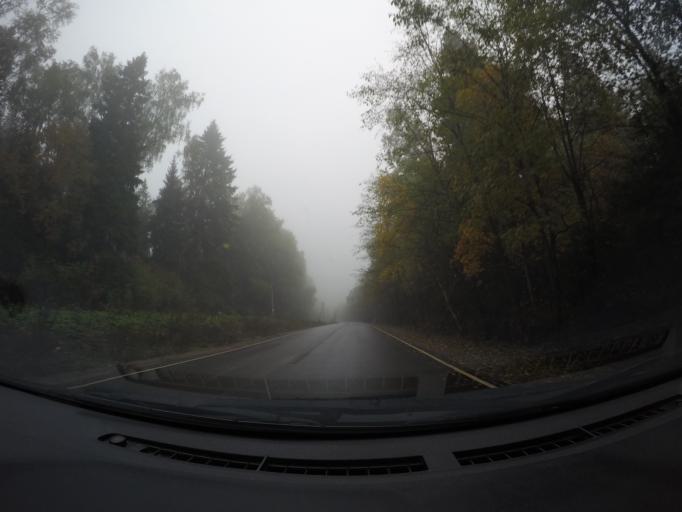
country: RU
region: Moskovskaya
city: Ruza
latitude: 55.7872
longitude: 36.2491
